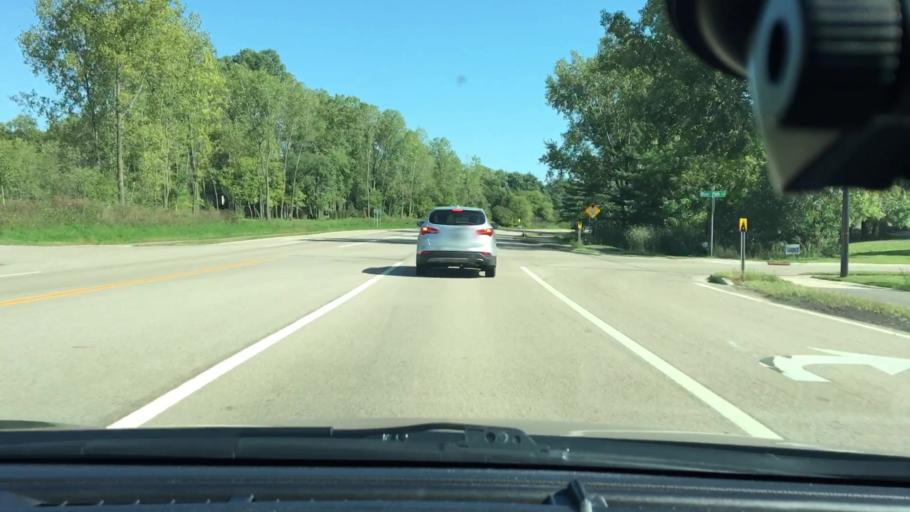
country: US
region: Minnesota
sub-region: Washington County
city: Stillwater
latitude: 45.0567
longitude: -92.8319
